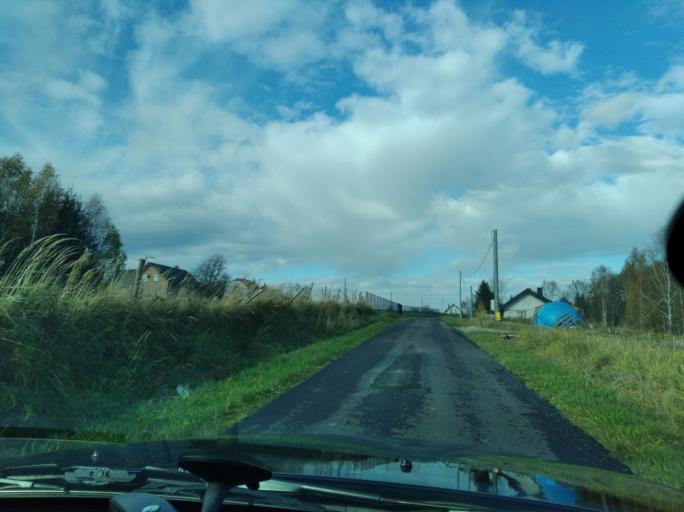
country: PL
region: Subcarpathian Voivodeship
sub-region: Powiat debicki
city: Debica
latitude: 50.0261
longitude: 21.4663
